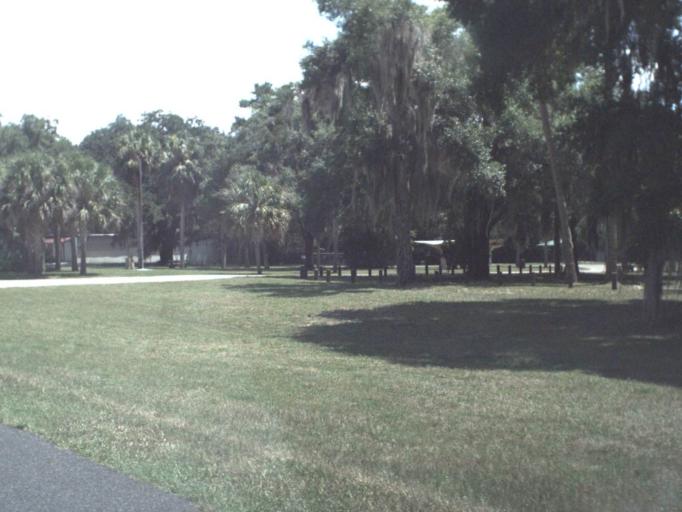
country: US
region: Florida
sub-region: Alachua County
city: Gainesville
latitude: 29.6174
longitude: -82.2556
